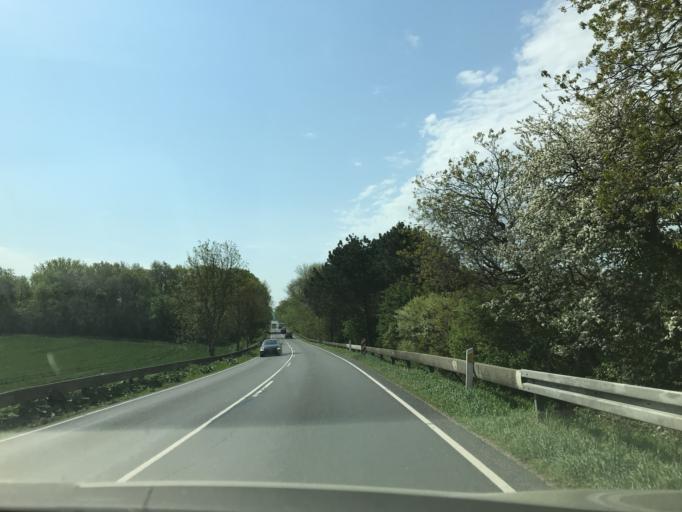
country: DK
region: South Denmark
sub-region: Assens Kommune
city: Assens
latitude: 55.3454
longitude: 9.9374
